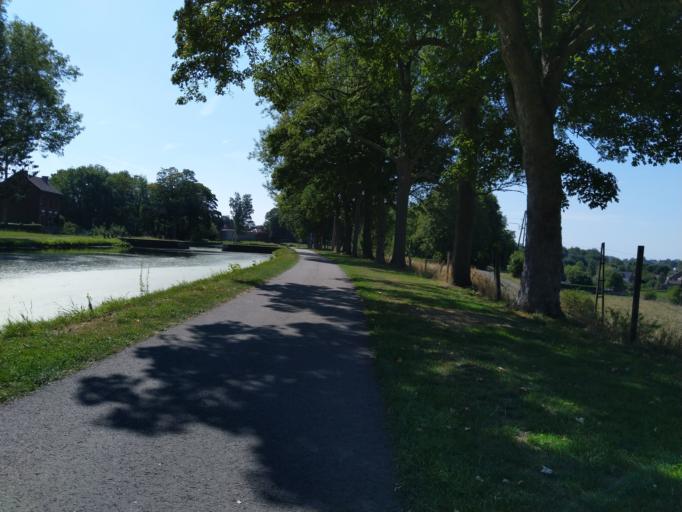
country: BE
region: Wallonia
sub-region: Province du Hainaut
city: Roeulx
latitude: 50.4745
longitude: 4.1142
